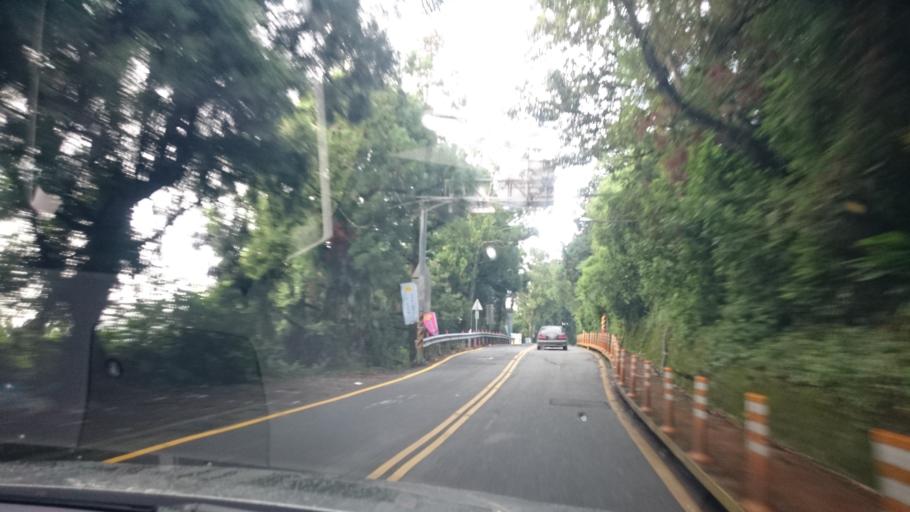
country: TW
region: Taiwan
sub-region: Nantou
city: Puli
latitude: 24.0456
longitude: 121.1578
